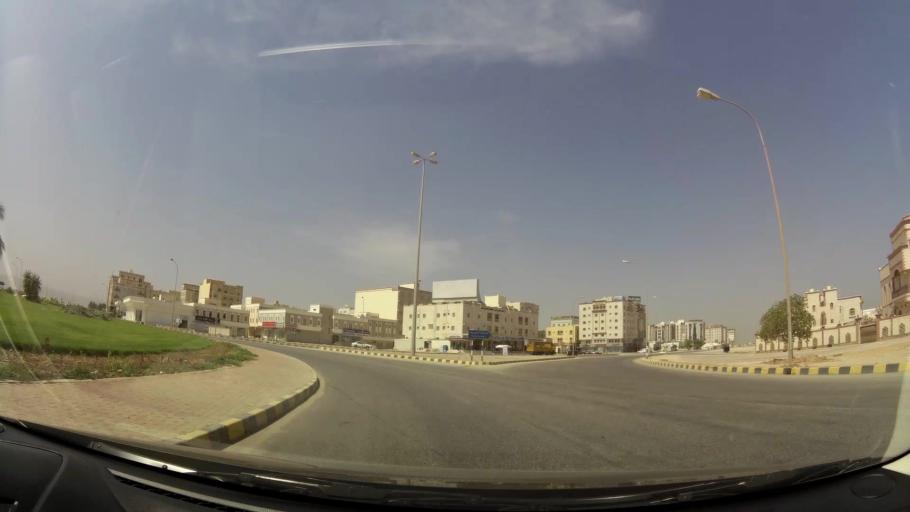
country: OM
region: Zufar
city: Salalah
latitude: 17.0500
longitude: 54.1493
